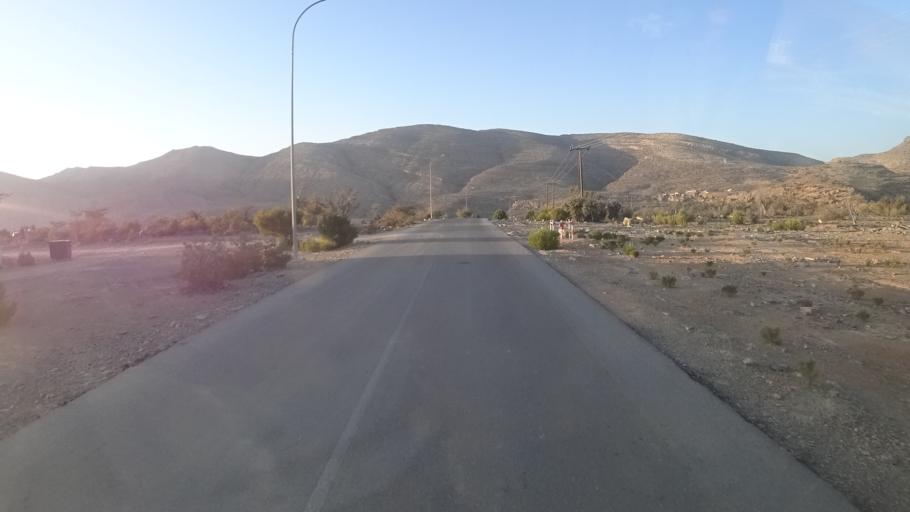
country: OM
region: Al Batinah
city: Bayt al `Awabi
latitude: 23.1447
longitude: 57.5389
